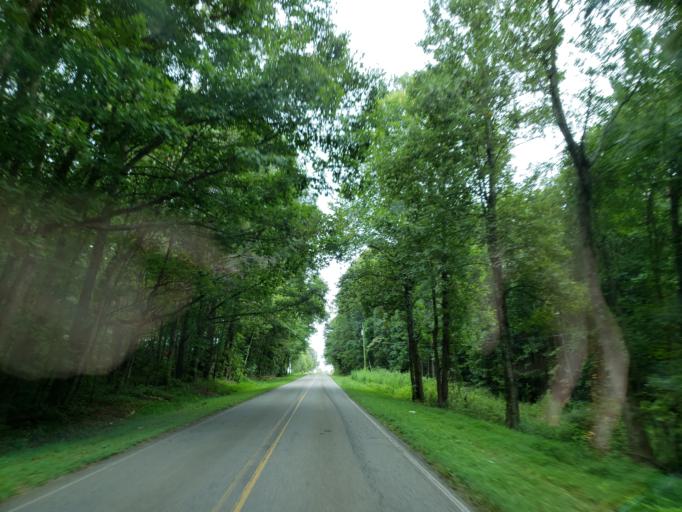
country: US
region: Georgia
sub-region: Pickens County
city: Jasper
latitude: 34.5017
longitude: -84.5216
